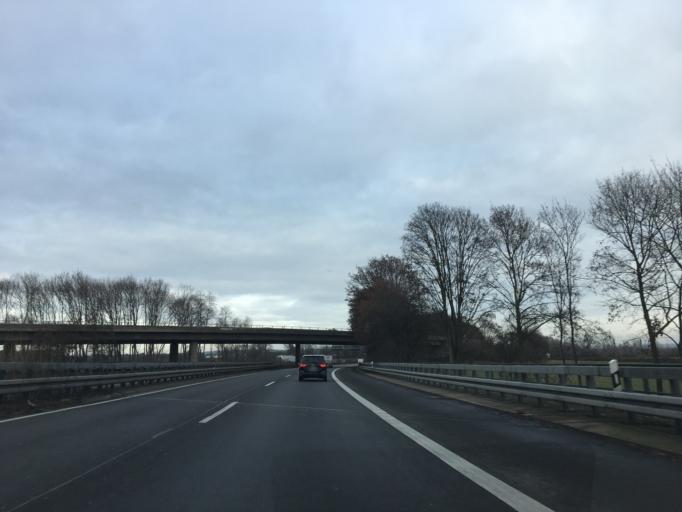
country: DE
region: North Rhine-Westphalia
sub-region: Regierungsbezirk Koln
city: Troisdorf
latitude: 50.7642
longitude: 7.1385
